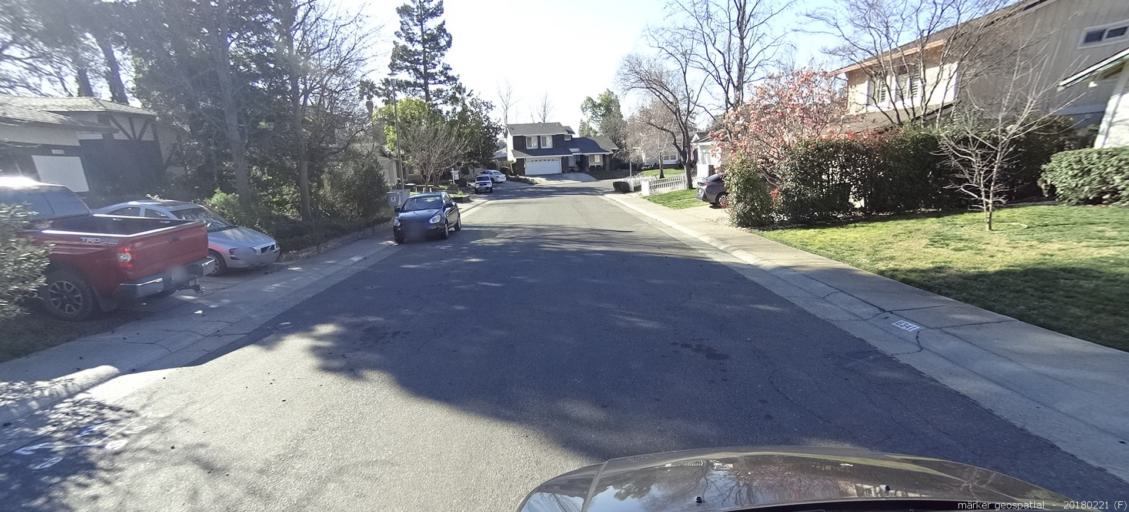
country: US
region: California
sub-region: Sacramento County
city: Orangevale
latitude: 38.6818
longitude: -121.2519
